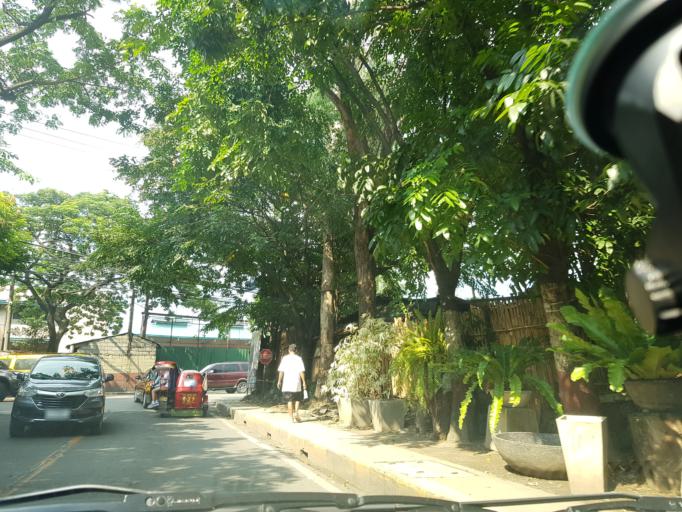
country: PH
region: Metro Manila
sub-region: Pasig
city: Pasig City
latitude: 14.5751
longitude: 121.0895
